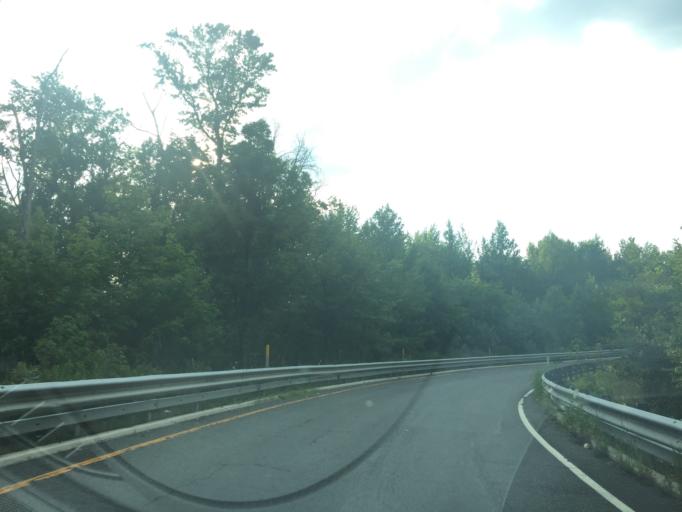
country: US
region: New Jersey
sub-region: Mercer County
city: Hightstown
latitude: 40.2813
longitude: -74.5313
